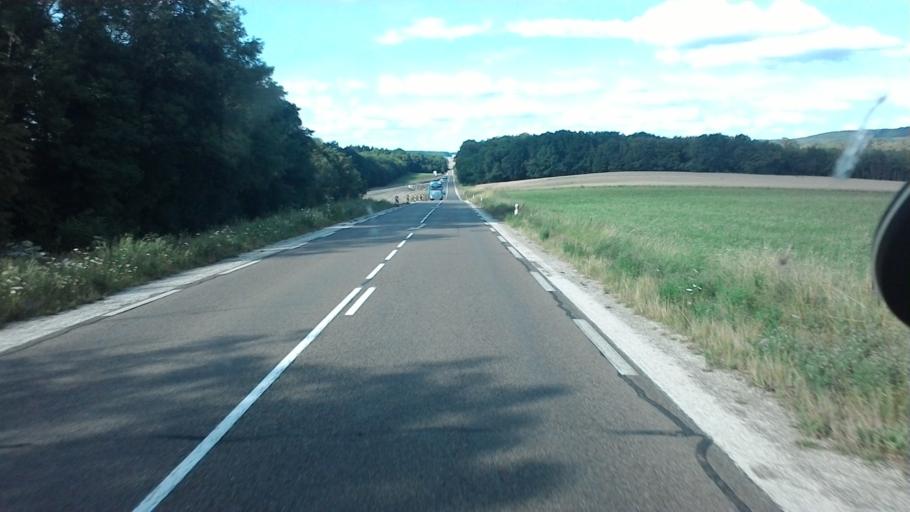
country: FR
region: Franche-Comte
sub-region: Departement de la Haute-Saone
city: Frotey-les-Vesoul
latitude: 47.7030
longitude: 6.2902
